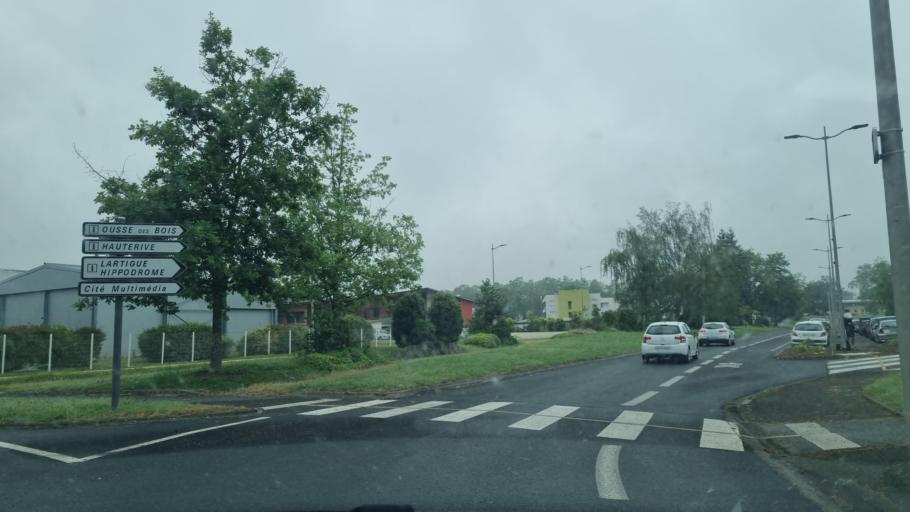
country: FR
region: Aquitaine
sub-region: Departement des Pyrenees-Atlantiques
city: Idron
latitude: 43.3206
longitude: -0.3274
